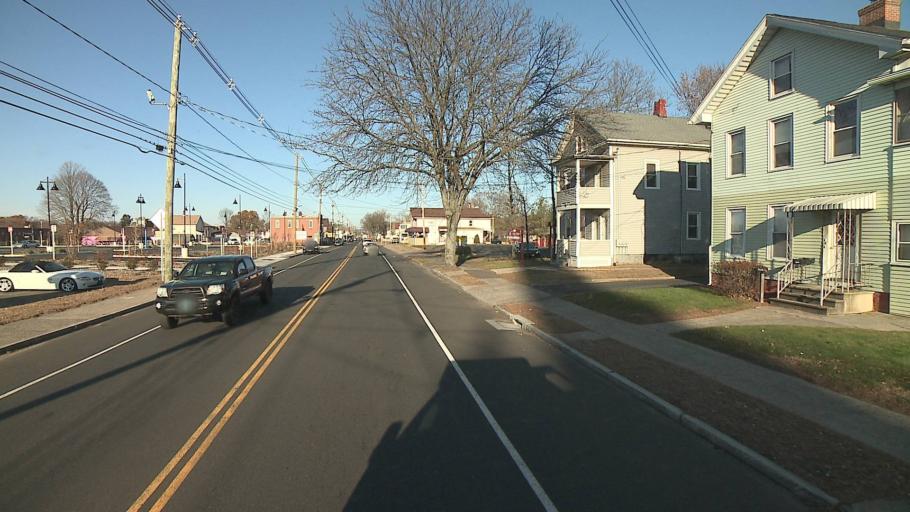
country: US
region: Connecticut
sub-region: New Haven County
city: Wallingford
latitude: 41.4590
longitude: -72.8228
